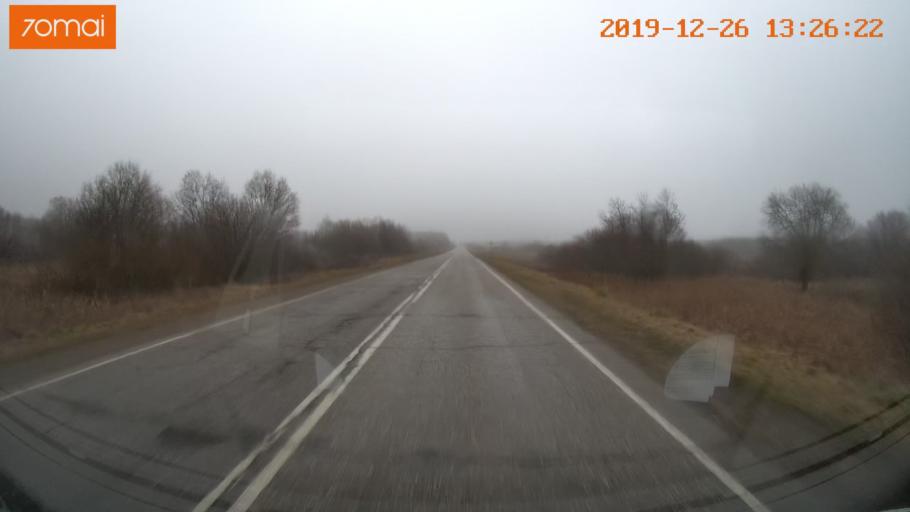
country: RU
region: Vologda
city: Cherepovets
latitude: 58.8650
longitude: 38.2247
